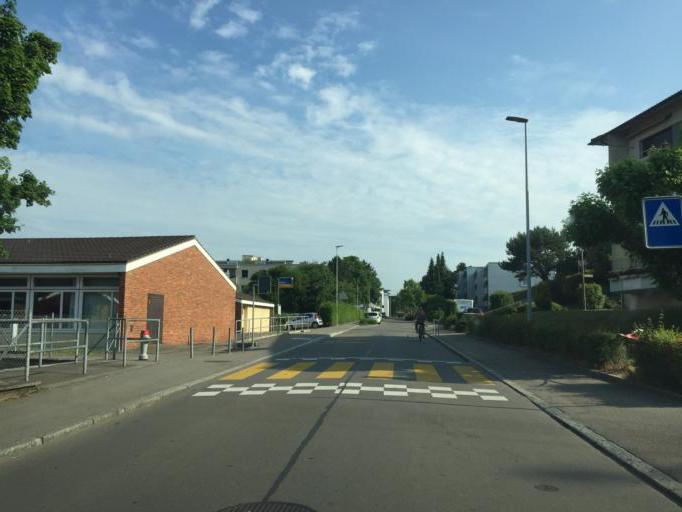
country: CH
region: Zurich
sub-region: Bezirk Buelach
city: Buelach / Soligaenter
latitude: 47.5265
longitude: 8.5443
